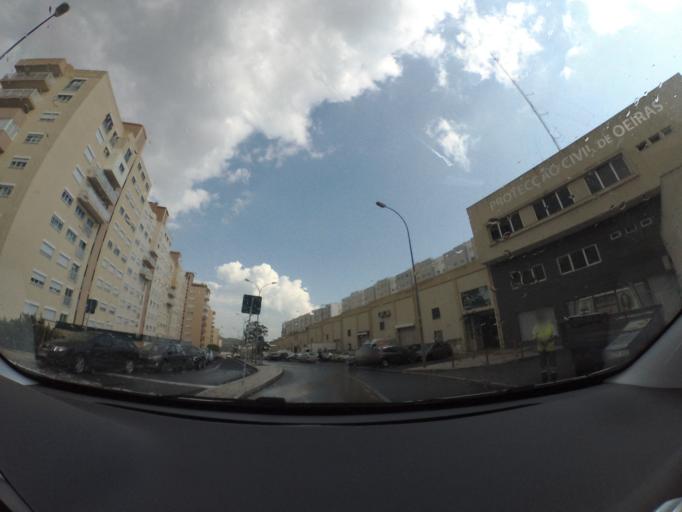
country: PT
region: Lisbon
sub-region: Oeiras
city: Linda-a-Velha
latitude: 38.7202
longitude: -9.2329
